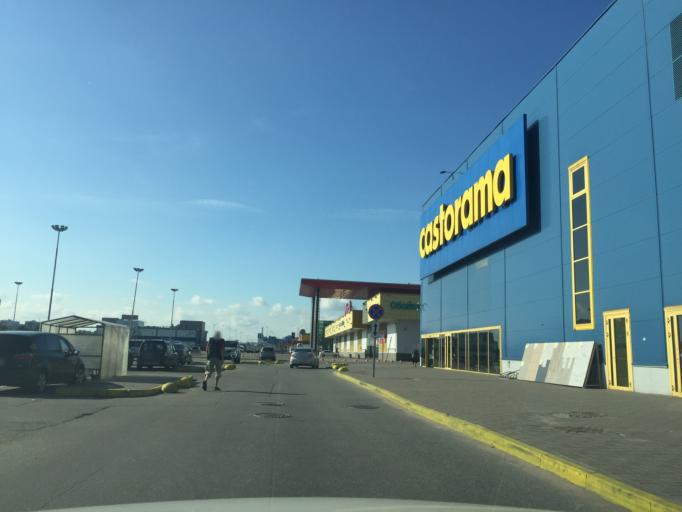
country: RU
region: St.-Petersburg
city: Kupchino
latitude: 59.8289
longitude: 30.3174
